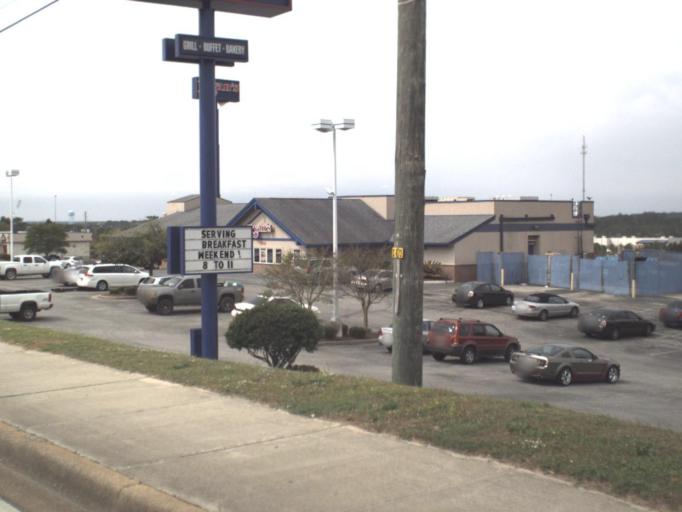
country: US
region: Florida
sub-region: Okaloosa County
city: Crestview
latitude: 30.7302
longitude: -86.5674
